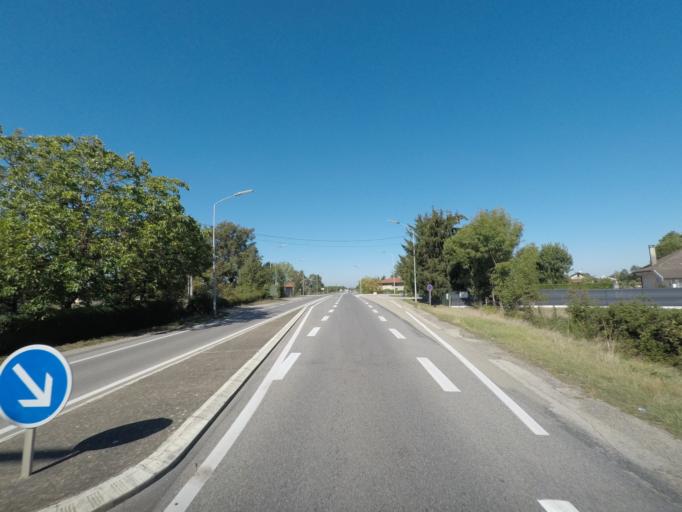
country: FR
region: Rhone-Alpes
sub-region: Departement de l'Ain
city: Viriat
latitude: 46.2511
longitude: 5.1841
